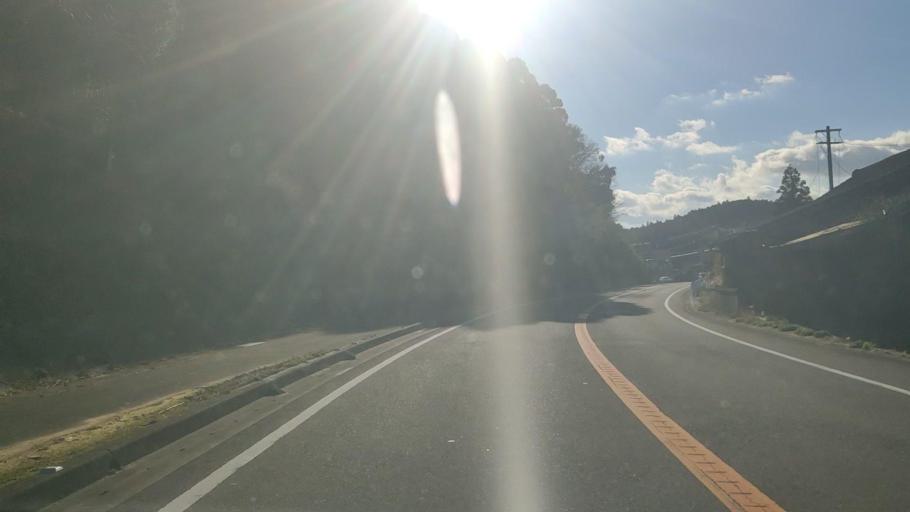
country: JP
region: Fukuoka
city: Maebaru-chuo
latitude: 33.4399
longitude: 130.2662
